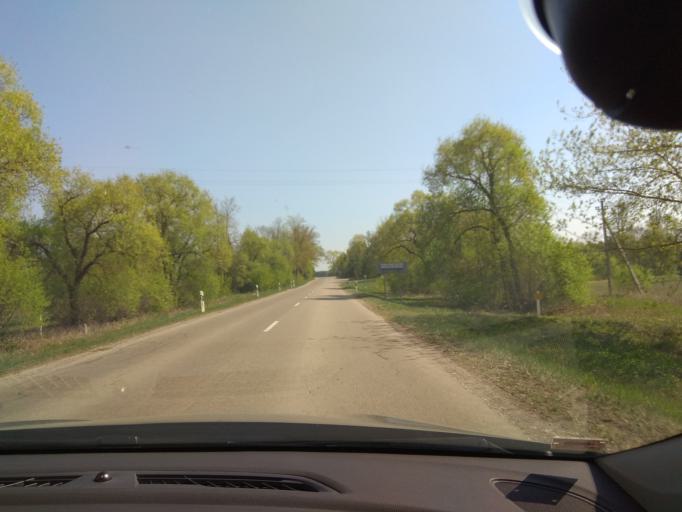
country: LT
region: Panevezys
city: Pasvalys
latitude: 55.9375
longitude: 24.2371
